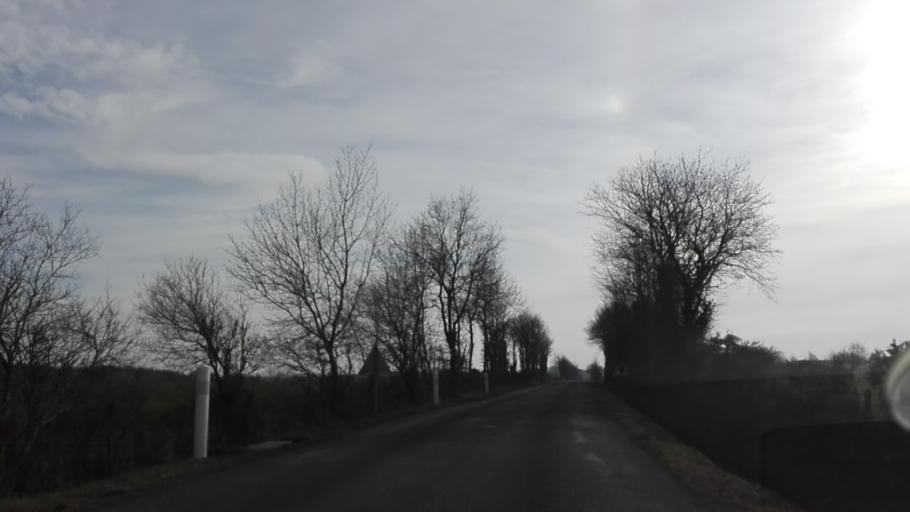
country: FR
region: Pays de la Loire
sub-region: Departement de la Vendee
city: Les Brouzils
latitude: 46.8936
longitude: -1.2932
